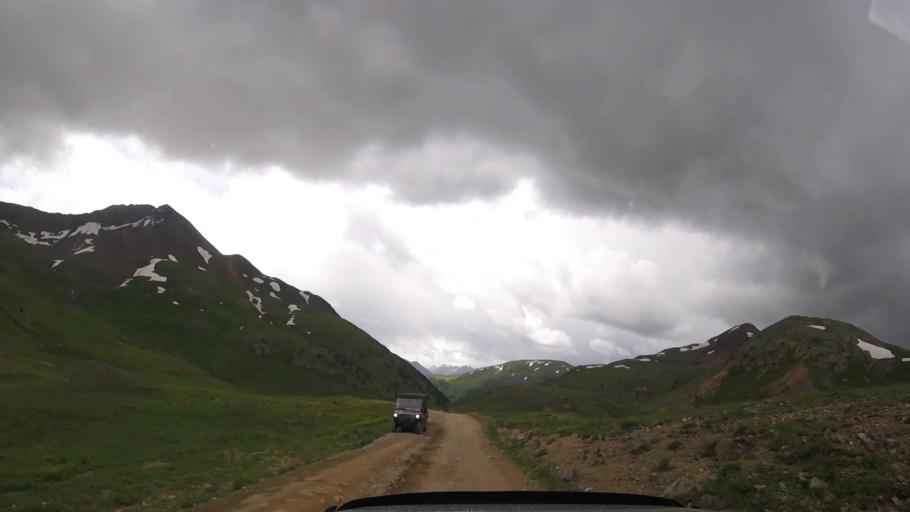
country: US
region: Colorado
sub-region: Ouray County
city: Ouray
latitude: 37.9543
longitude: -107.5748
